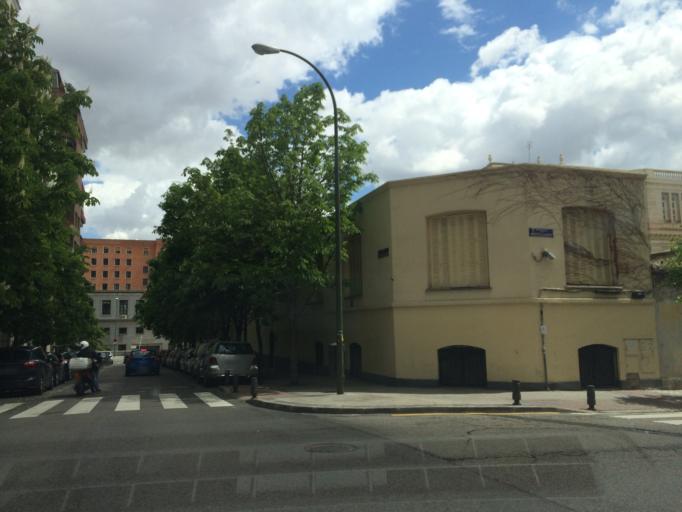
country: ES
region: Madrid
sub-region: Provincia de Madrid
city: Chamberi
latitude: 40.4429
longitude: -3.6960
